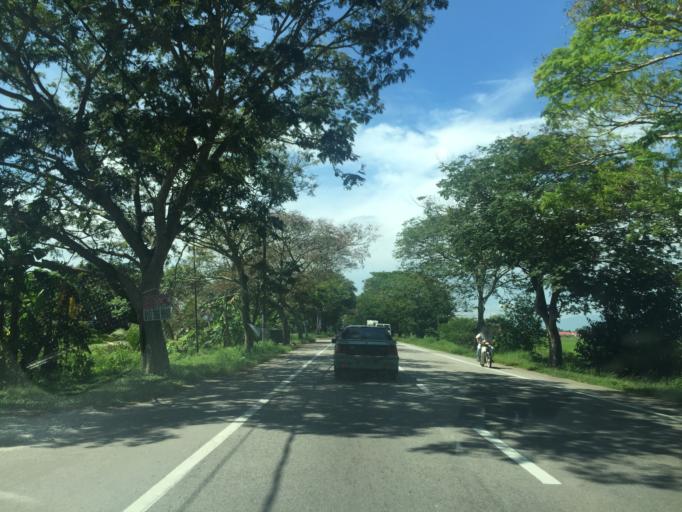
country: MY
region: Penang
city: Tasek Glugor
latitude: 5.4599
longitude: 100.4474
